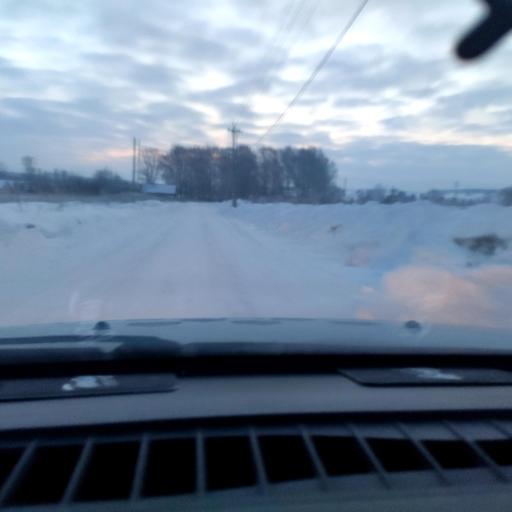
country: RU
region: Perm
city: Kultayevo
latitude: 57.8736
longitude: 55.9836
